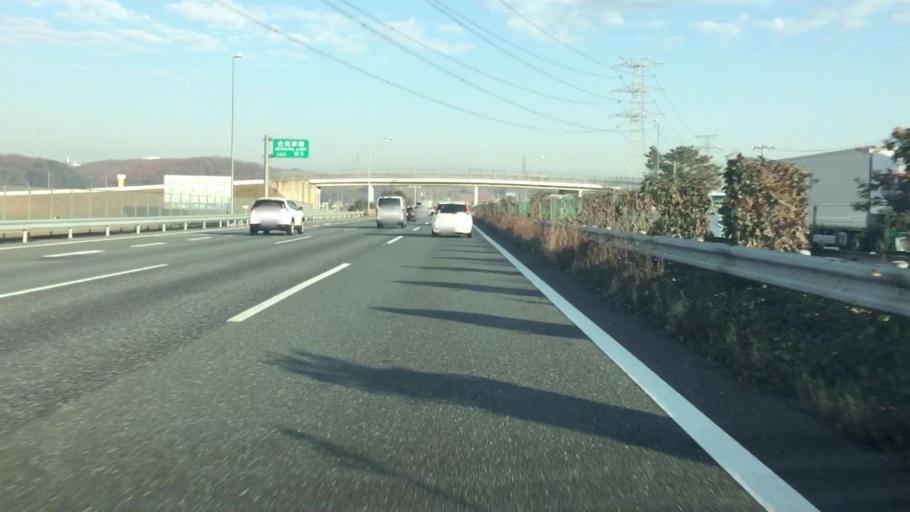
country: JP
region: Saitama
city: Sakado
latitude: 35.9721
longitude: 139.3801
